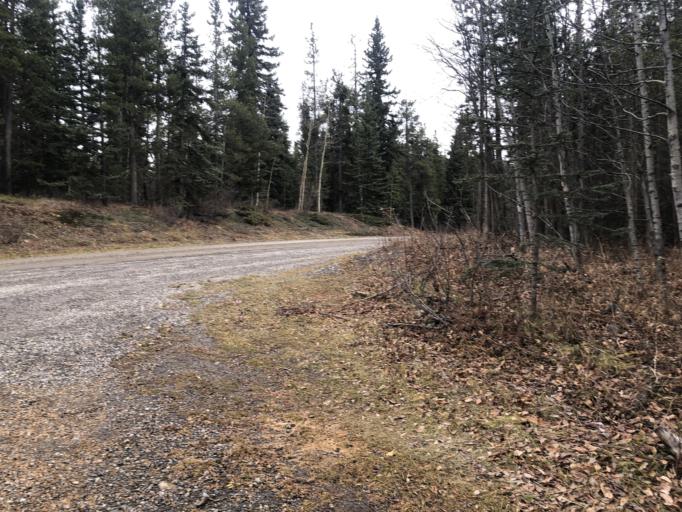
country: CA
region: Alberta
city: Cochrane
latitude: 51.0288
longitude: -114.8698
